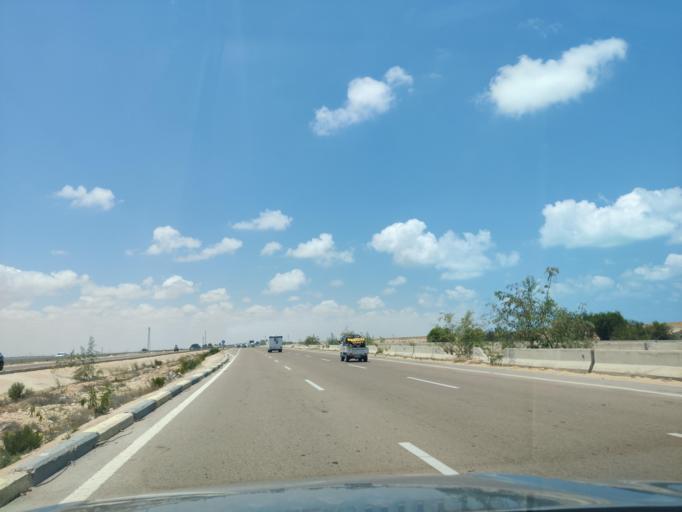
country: EG
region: Muhafazat Matruh
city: Al `Alamayn
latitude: 30.8125
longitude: 29.0804
